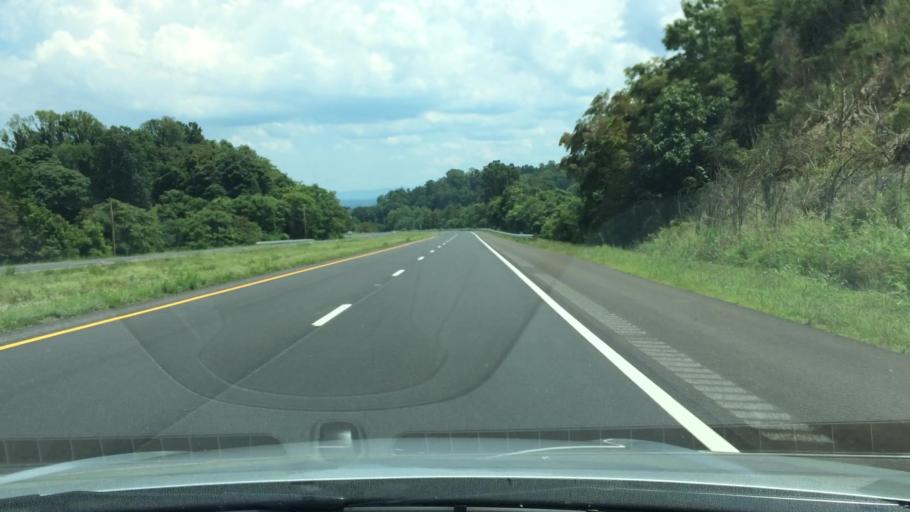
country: US
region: Tennessee
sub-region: Hamblen County
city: Morristown
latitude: 36.1875
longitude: -83.2591
